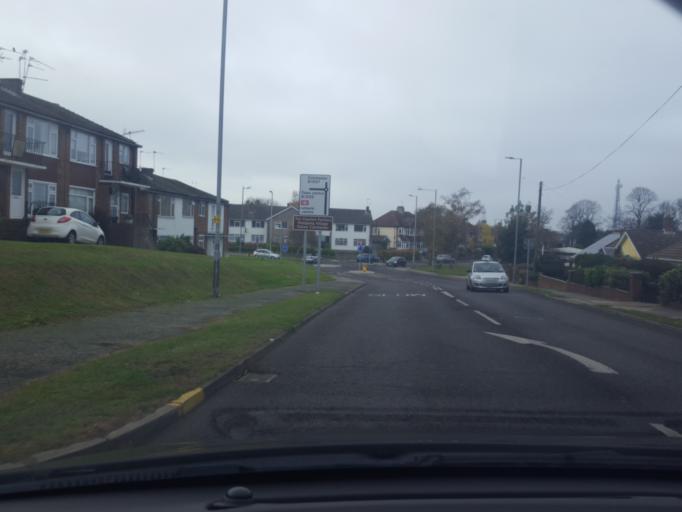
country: GB
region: England
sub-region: Essex
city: Clacton-on-Sea
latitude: 51.8023
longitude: 1.1727
